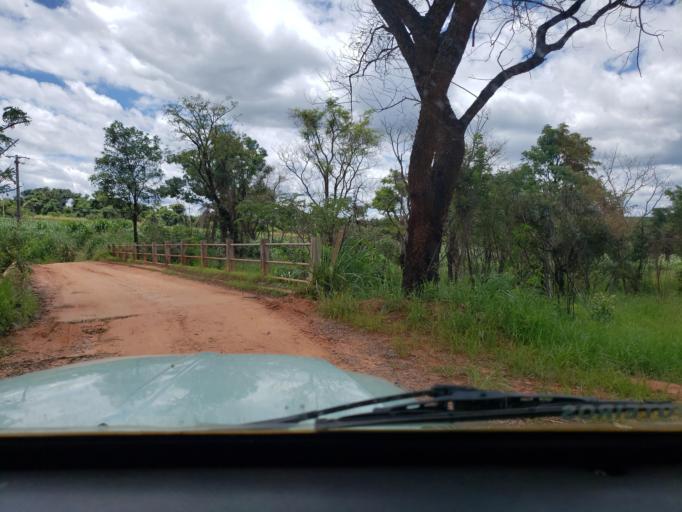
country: BR
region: Sao Paulo
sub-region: Aguai
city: Aguai
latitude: -22.1870
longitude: -46.9500
